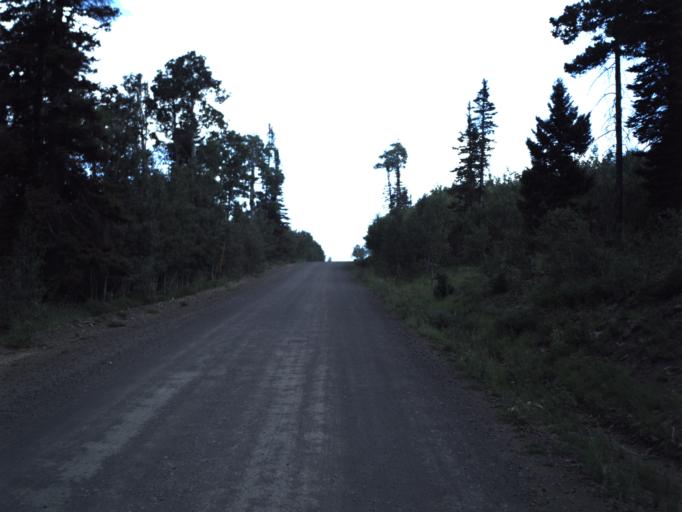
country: US
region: Utah
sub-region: Piute County
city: Junction
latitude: 38.2470
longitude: -112.3414
